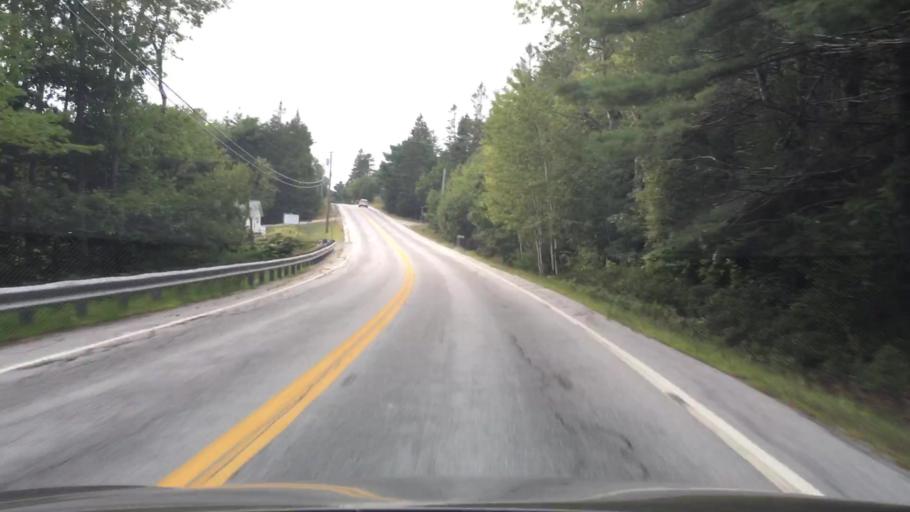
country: US
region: Maine
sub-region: Hancock County
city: Penobscot
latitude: 44.4463
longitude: -68.6136
